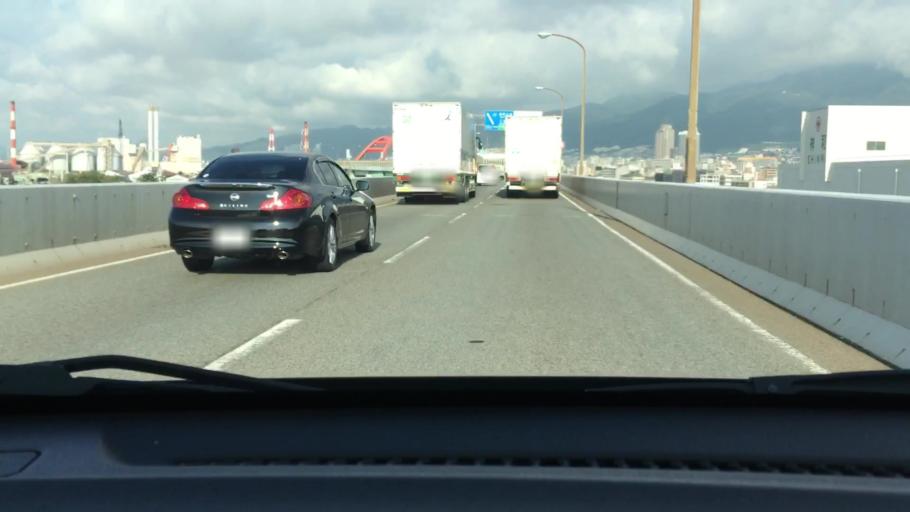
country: JP
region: Hyogo
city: Ashiya
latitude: 34.7064
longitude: 135.2617
